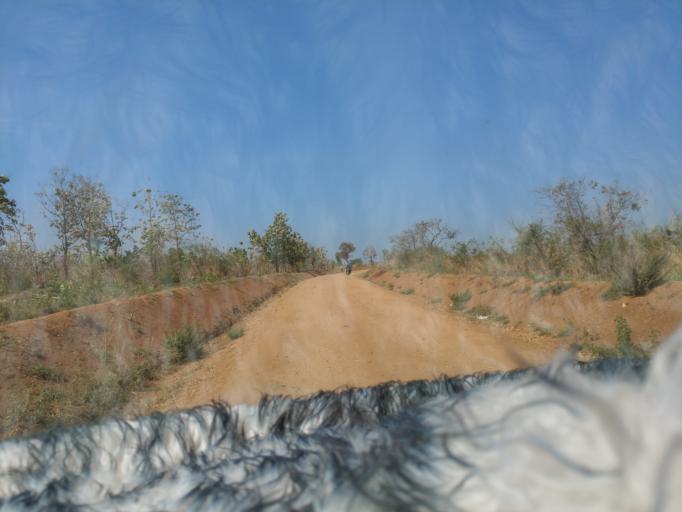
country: UG
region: Northern Region
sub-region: Yumbe District
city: Yumbe
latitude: 3.3899
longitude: 31.3355
